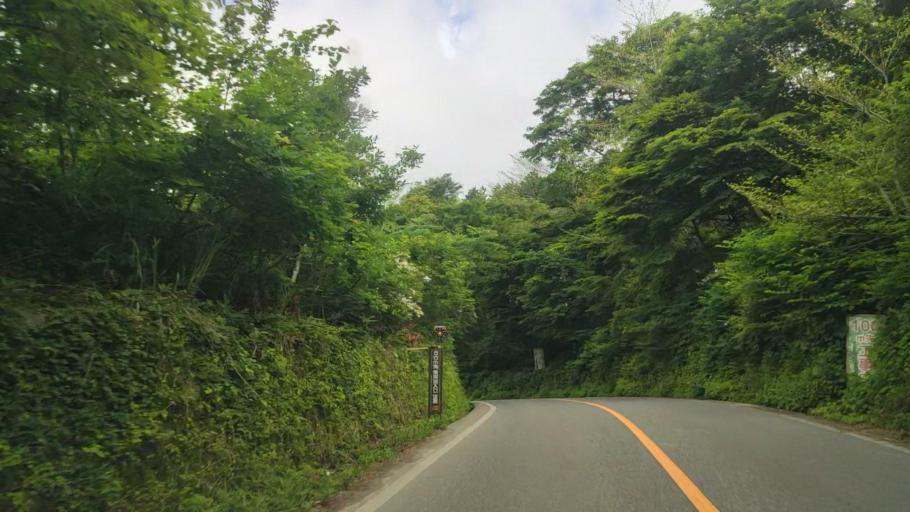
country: JP
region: Tottori
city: Yonago
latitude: 35.3583
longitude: 133.5310
